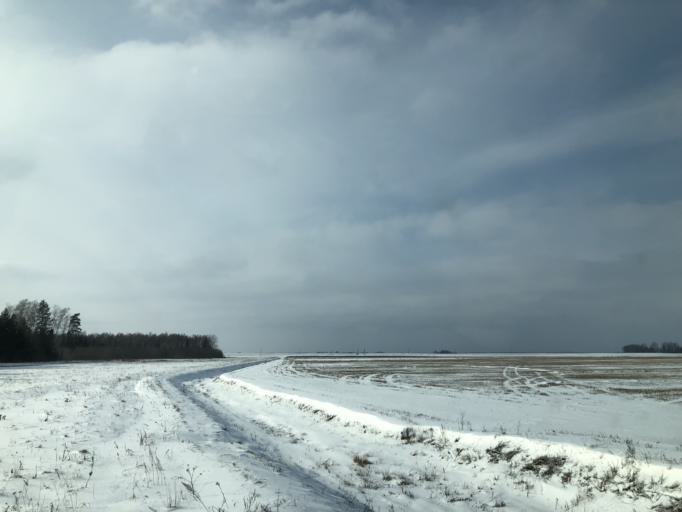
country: BY
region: Minsk
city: Kapyl'
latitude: 53.2813
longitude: 27.0803
